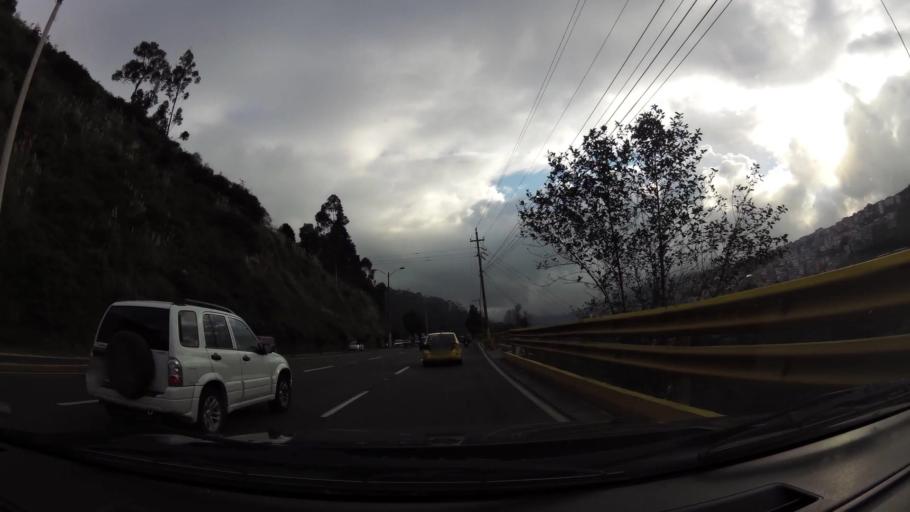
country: EC
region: Pichincha
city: Quito
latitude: -0.2294
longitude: -78.4969
